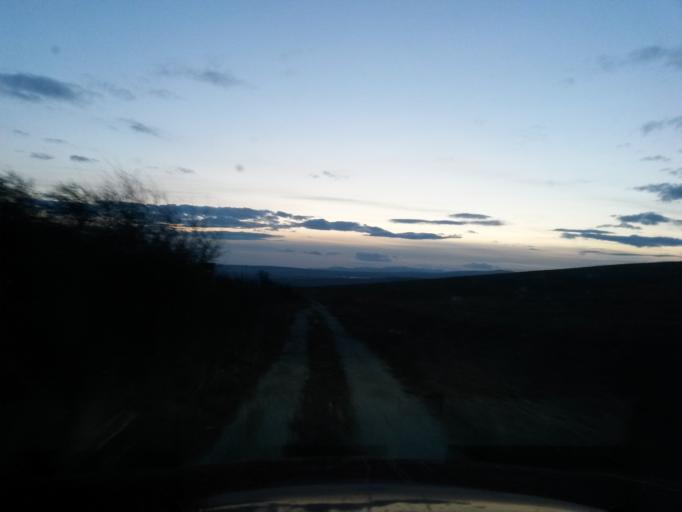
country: SK
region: Kosicky
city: Kosice
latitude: 48.6891
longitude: 21.3666
